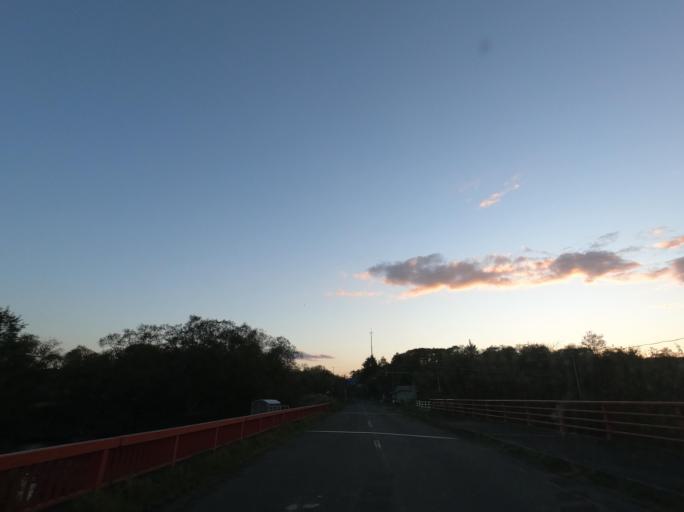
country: JP
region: Hokkaido
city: Kushiro
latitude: 43.2205
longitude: 144.4317
